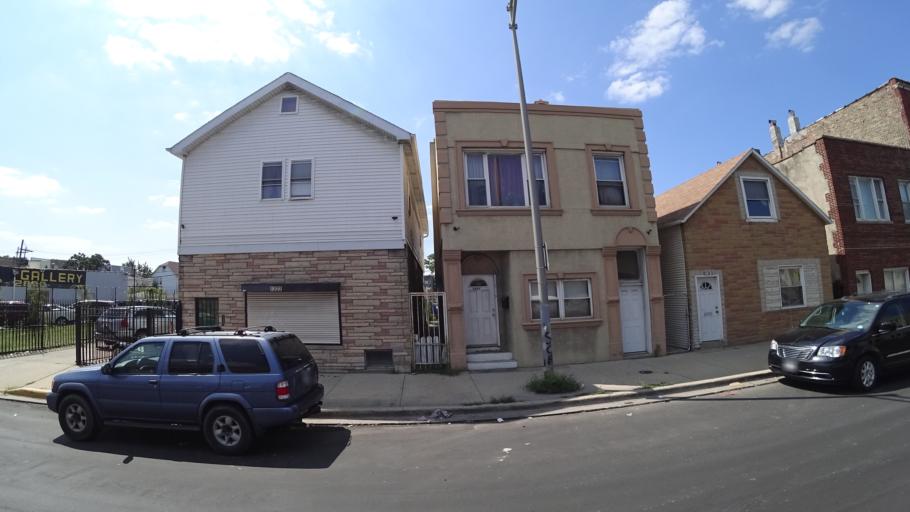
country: US
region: Illinois
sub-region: Cook County
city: Cicero
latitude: 41.8633
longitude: -87.7447
